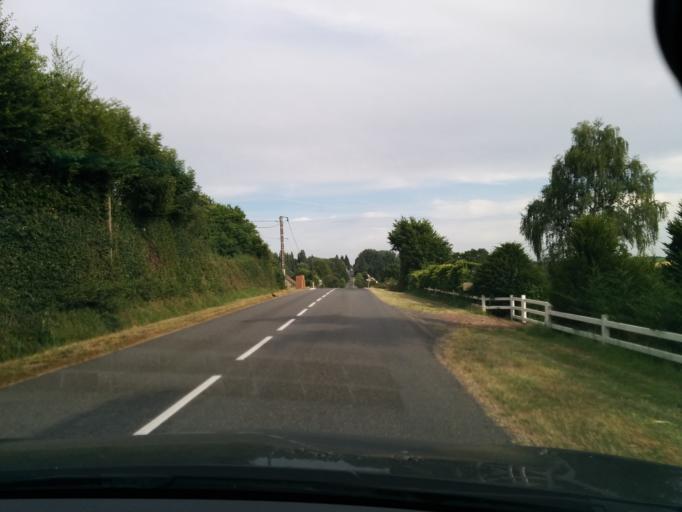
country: FR
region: Centre
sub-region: Departement du Cher
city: Savigny-en-Sancerre
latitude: 47.3910
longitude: 2.6871
